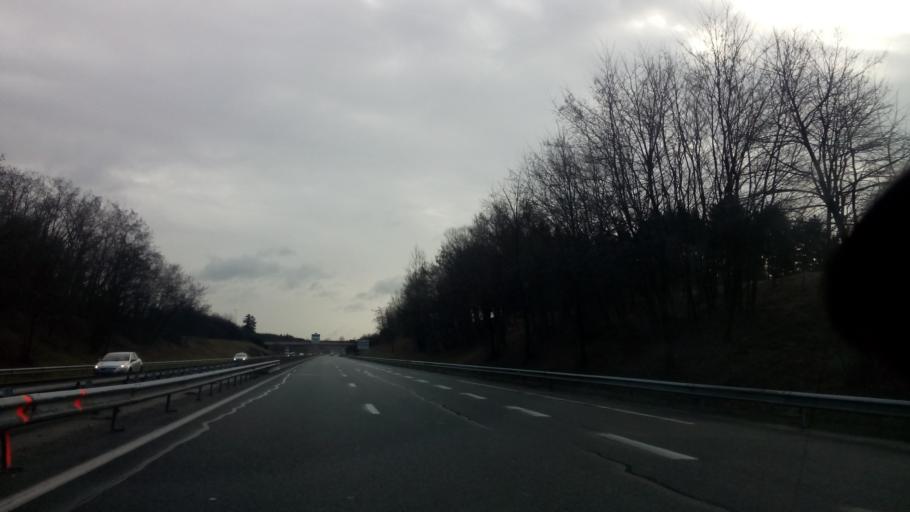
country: FR
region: Rhone-Alpes
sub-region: Departement du Rhone
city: Corbas
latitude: 45.6812
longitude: 4.8905
